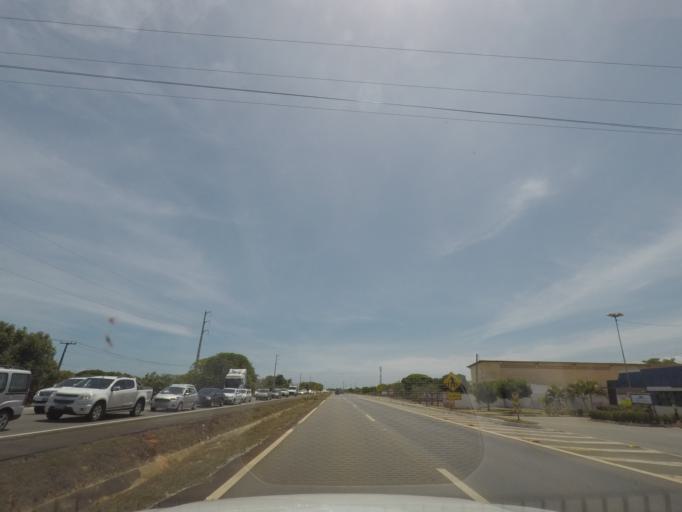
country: BR
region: Bahia
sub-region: Mata De Sao Joao
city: Mata de Sao Joao
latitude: -12.6297
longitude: -38.0646
